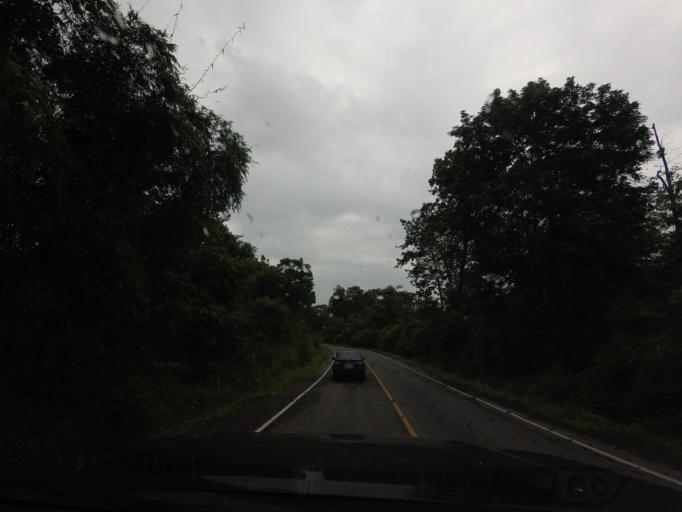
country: TH
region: Nong Khai
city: Sangkhom
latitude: 18.0382
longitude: 102.3223
